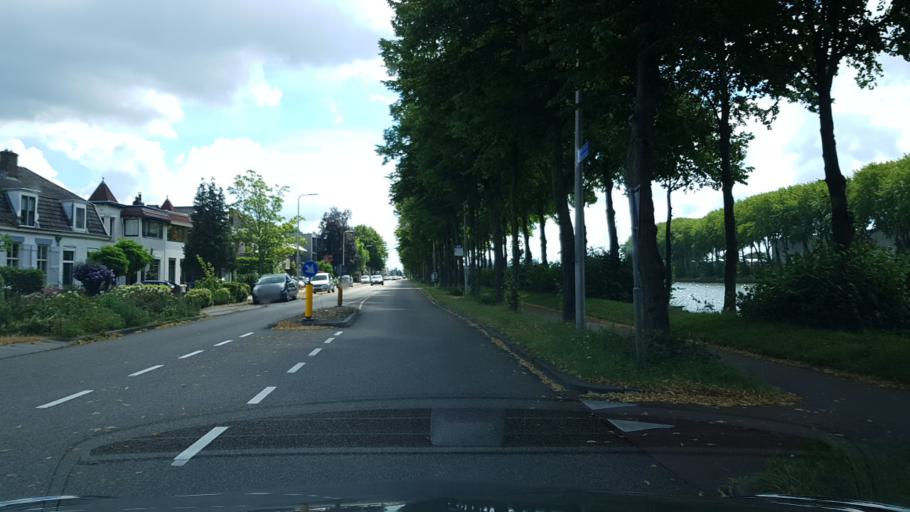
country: NL
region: Utrecht
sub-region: Stichtse Vecht
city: Maarssen
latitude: 52.1172
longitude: 5.0714
